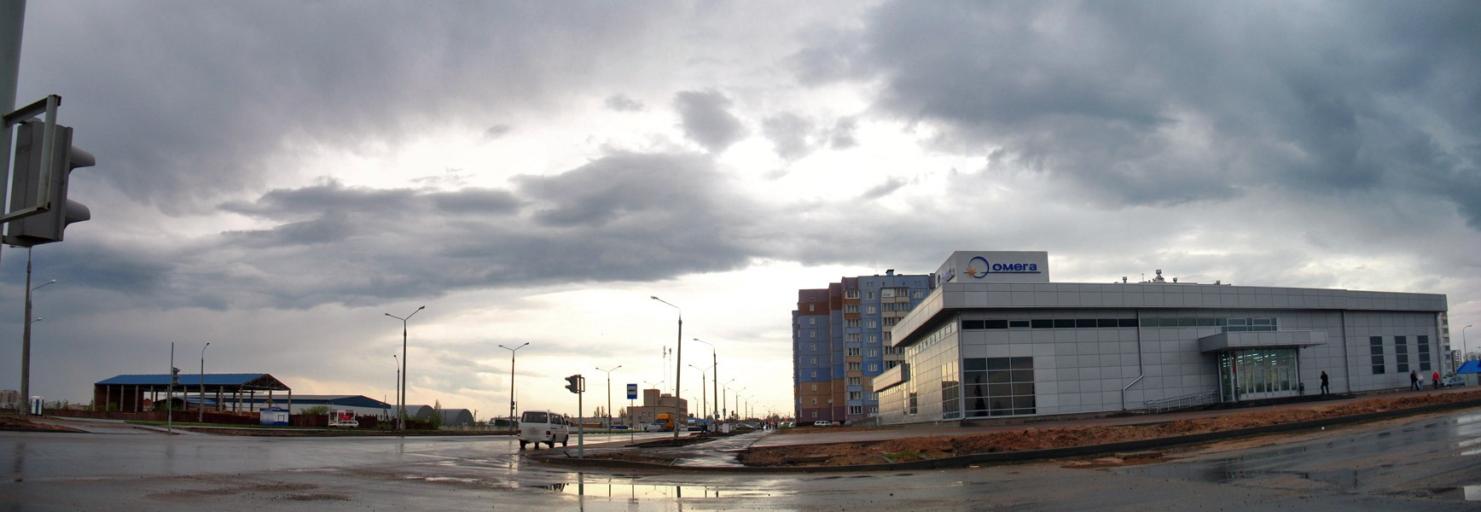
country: BY
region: Vitebsk
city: Vitebsk
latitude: 55.1661
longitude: 30.2555
